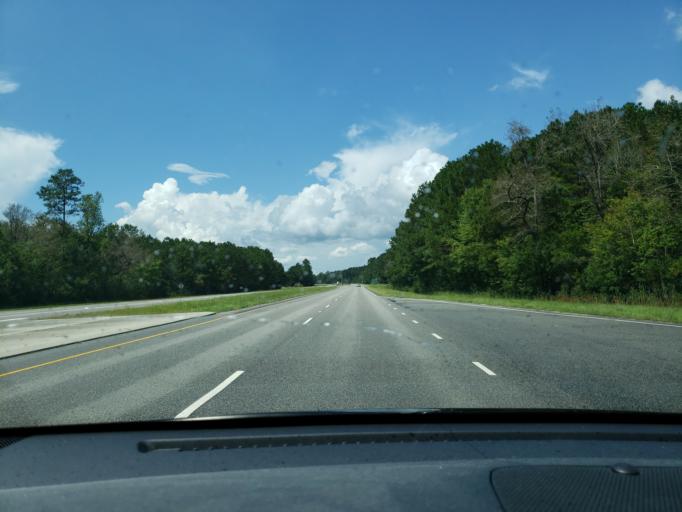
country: US
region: North Carolina
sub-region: Bladen County
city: Elizabethtown
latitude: 34.6405
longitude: -78.6724
